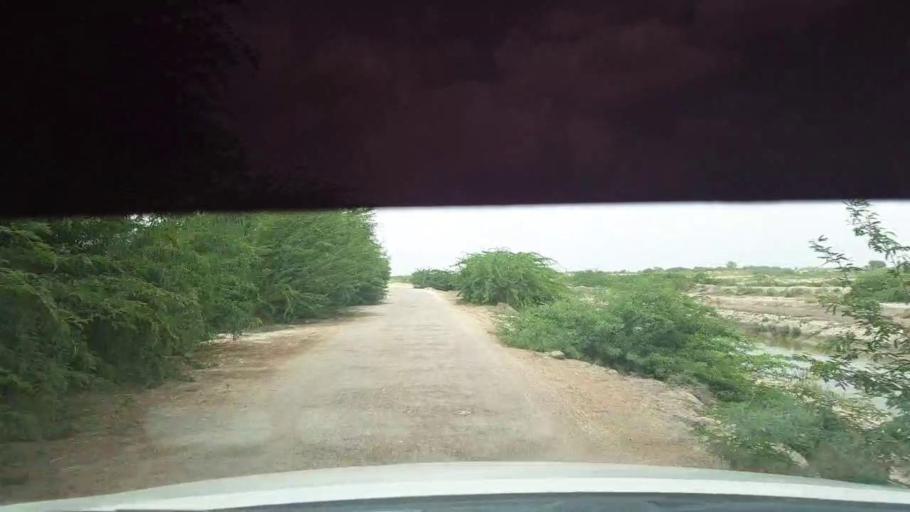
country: PK
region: Sindh
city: Kadhan
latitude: 24.4827
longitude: 69.0665
